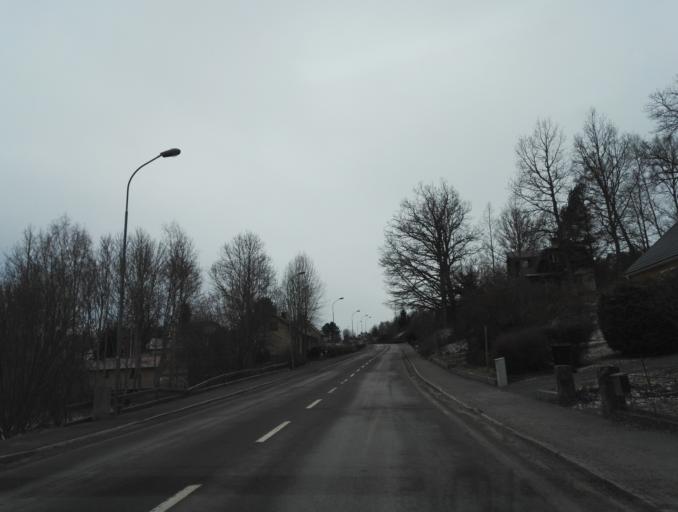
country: SE
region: Kalmar
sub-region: Hultsfreds Kommun
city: Virserum
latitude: 57.3141
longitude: 15.5851
